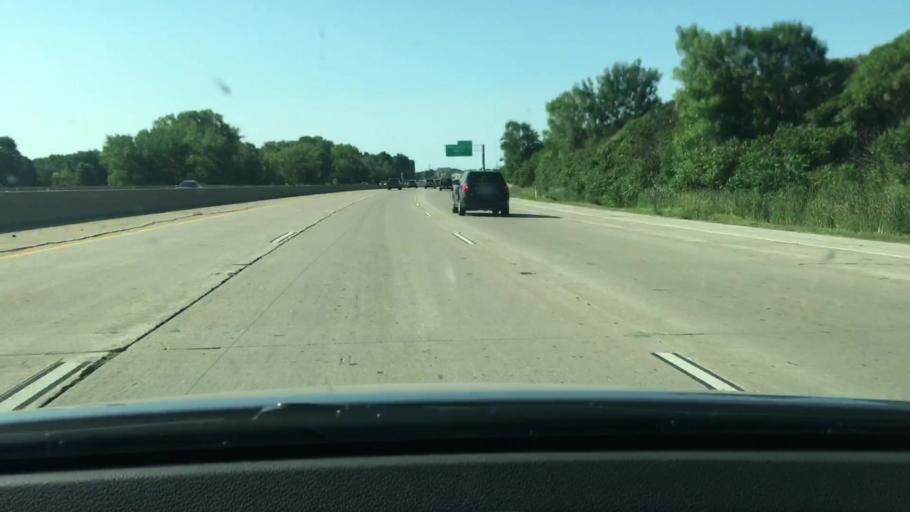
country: US
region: Wisconsin
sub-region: Winnebago County
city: Neenah
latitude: 44.1692
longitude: -88.4854
